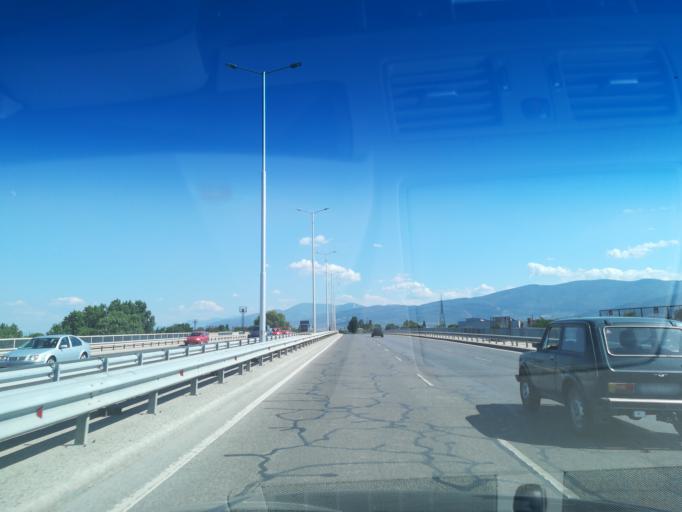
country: BG
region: Plovdiv
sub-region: Obshtina Plovdiv
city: Plovdiv
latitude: 42.1179
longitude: 24.7764
